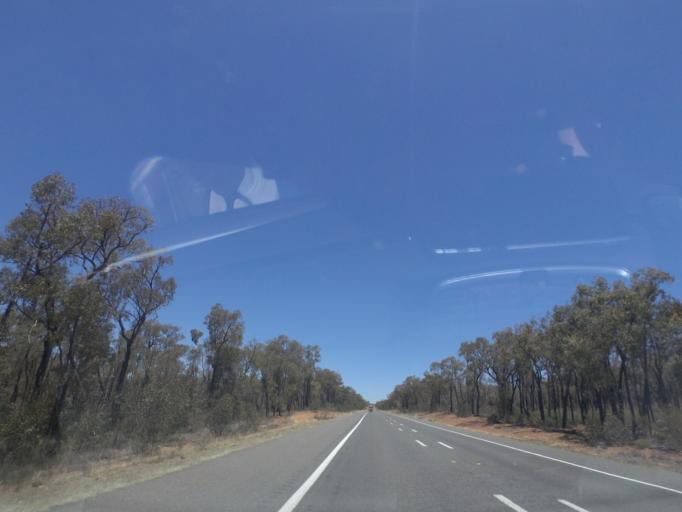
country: AU
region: New South Wales
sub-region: Warrumbungle Shire
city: Coonabarabran
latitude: -30.9088
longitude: 149.4367
